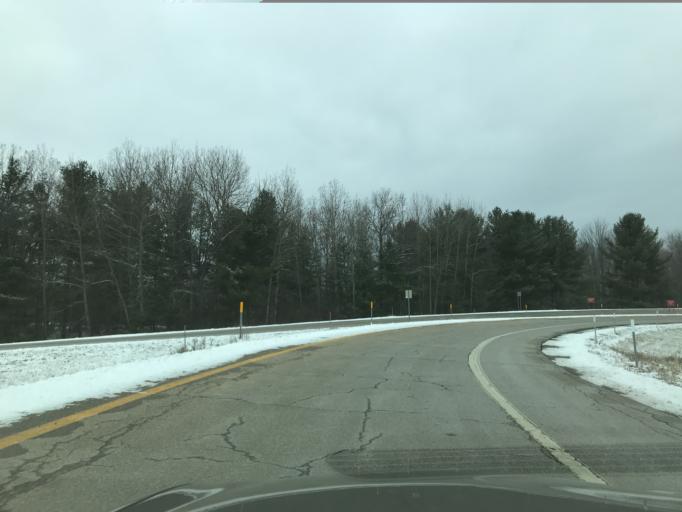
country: US
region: Michigan
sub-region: Roscommon County
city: Houghton Lake
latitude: 44.3360
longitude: -84.8092
